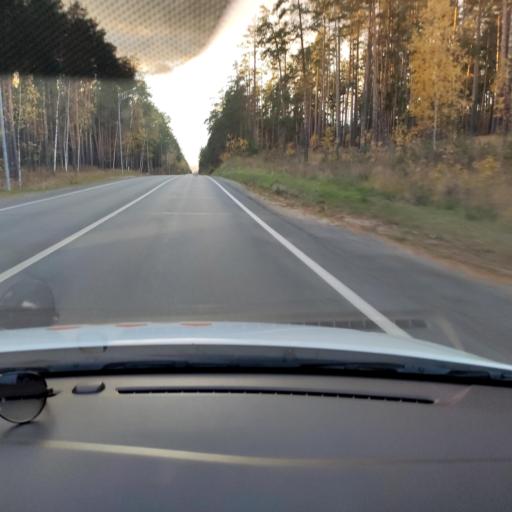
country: RU
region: Tatarstan
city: Verkhniy Uslon
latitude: 55.6373
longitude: 49.0543
